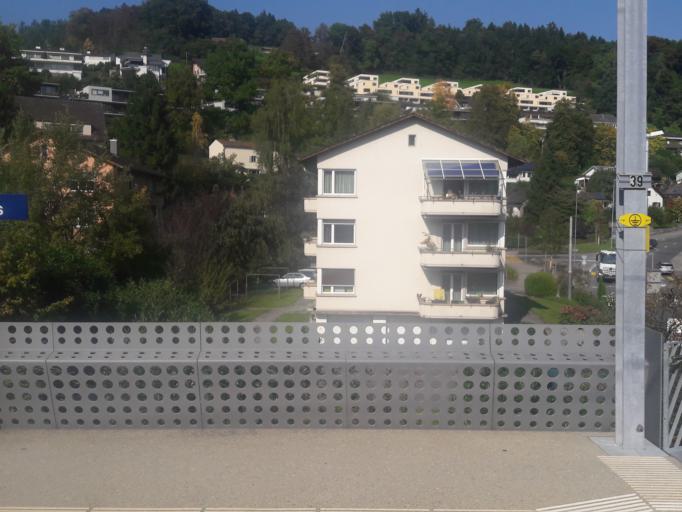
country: CH
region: Lucerne
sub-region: Lucerne-Land District
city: Adligenswil
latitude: 47.0537
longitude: 8.3387
